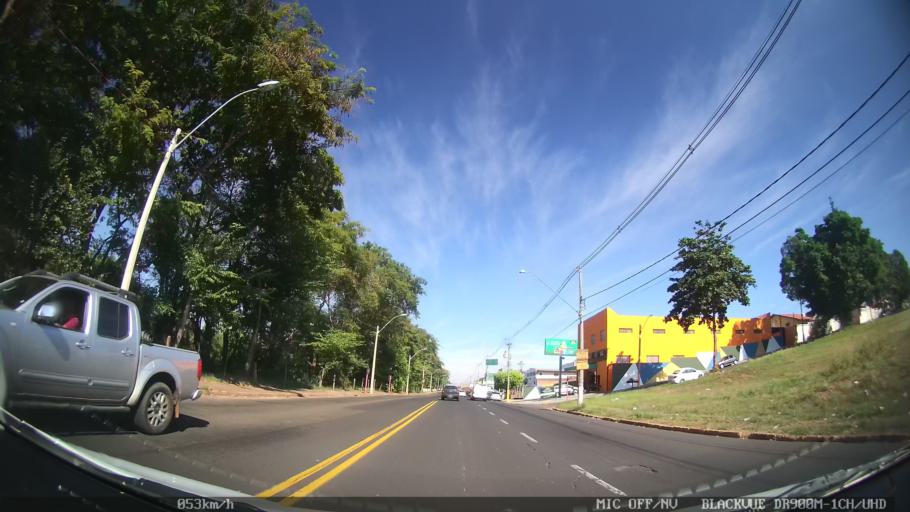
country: BR
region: Sao Paulo
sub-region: Sao Jose Do Rio Preto
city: Sao Jose do Rio Preto
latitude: -20.7856
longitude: -49.3849
